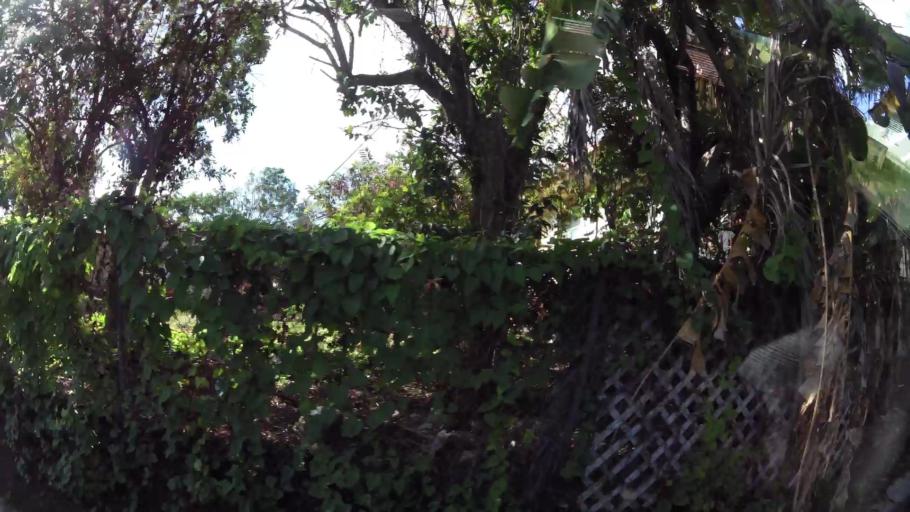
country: VG
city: Tortola
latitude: 18.4366
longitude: -64.5714
